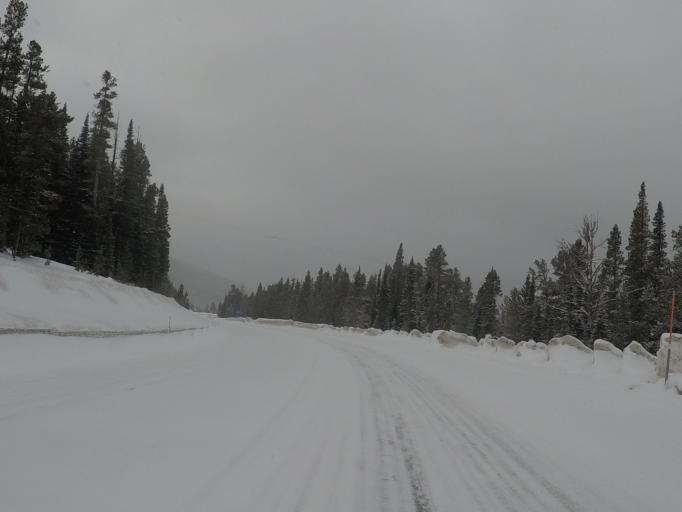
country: US
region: Montana
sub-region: Meagher County
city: White Sulphur Springs
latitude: 46.8400
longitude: -110.6960
